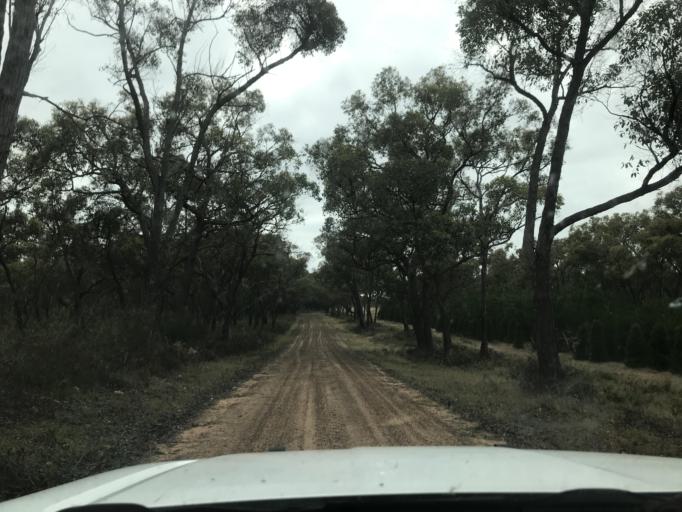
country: AU
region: South Australia
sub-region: Wattle Range
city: Penola
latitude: -37.1186
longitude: 141.1344
